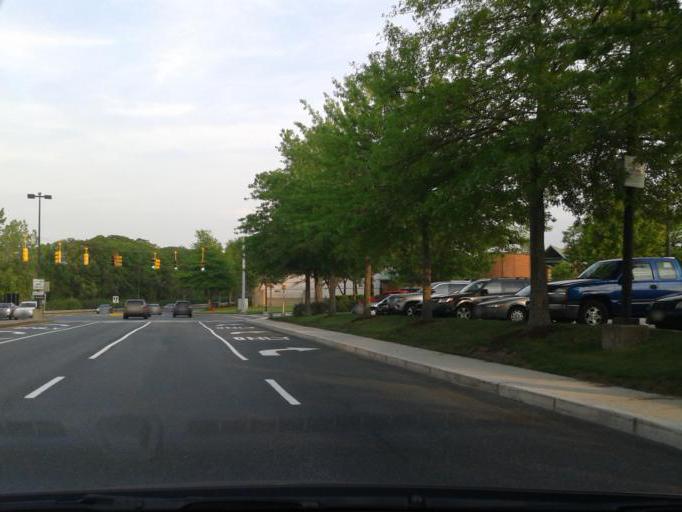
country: US
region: Massachusetts
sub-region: Middlesex County
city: Framingham
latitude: 42.3040
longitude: -71.3942
